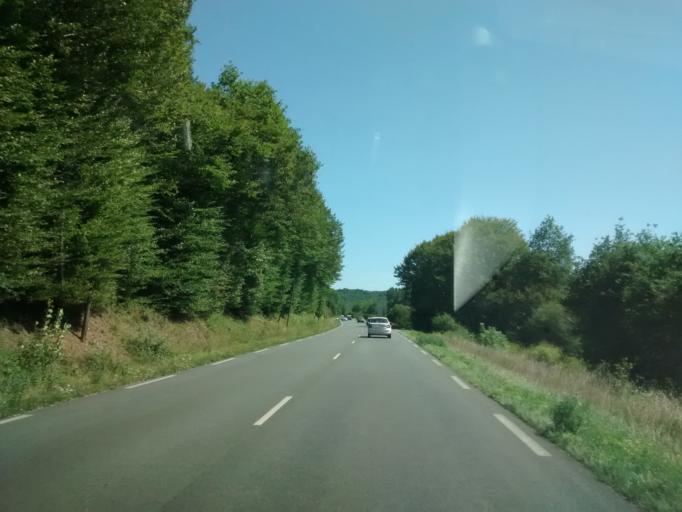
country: FR
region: Aquitaine
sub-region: Departement de la Dordogne
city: Bassillac
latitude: 45.1285
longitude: 0.8181
